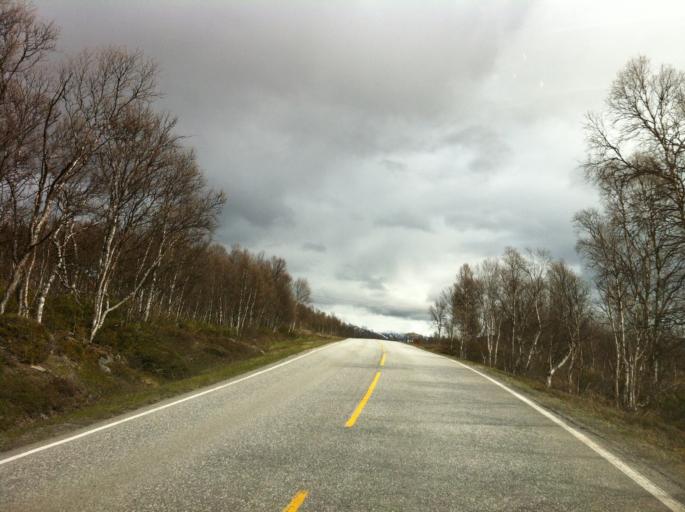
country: NO
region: Sor-Trondelag
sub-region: Roros
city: Roros
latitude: 62.6000
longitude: 11.5364
